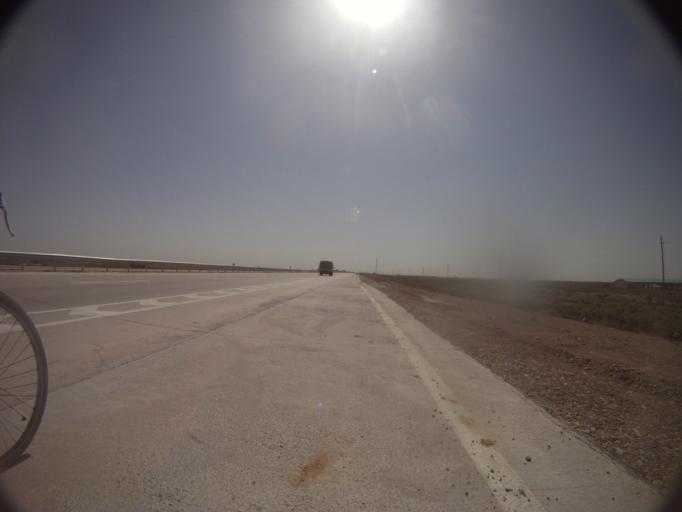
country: KZ
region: Ongtustik Qazaqstan
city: Khantaghy
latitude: 43.1249
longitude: 68.5975
